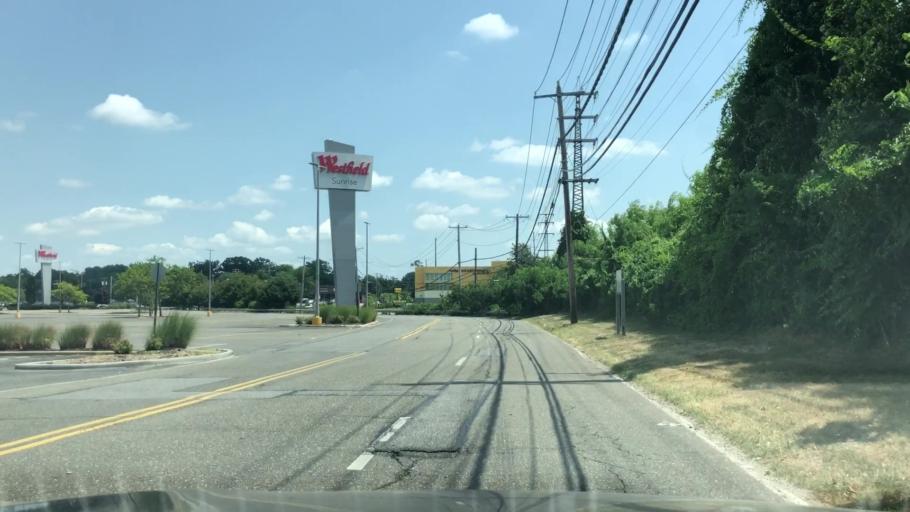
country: US
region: New York
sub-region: Nassau County
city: East Massapequa
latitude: 40.6793
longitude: -73.4349
